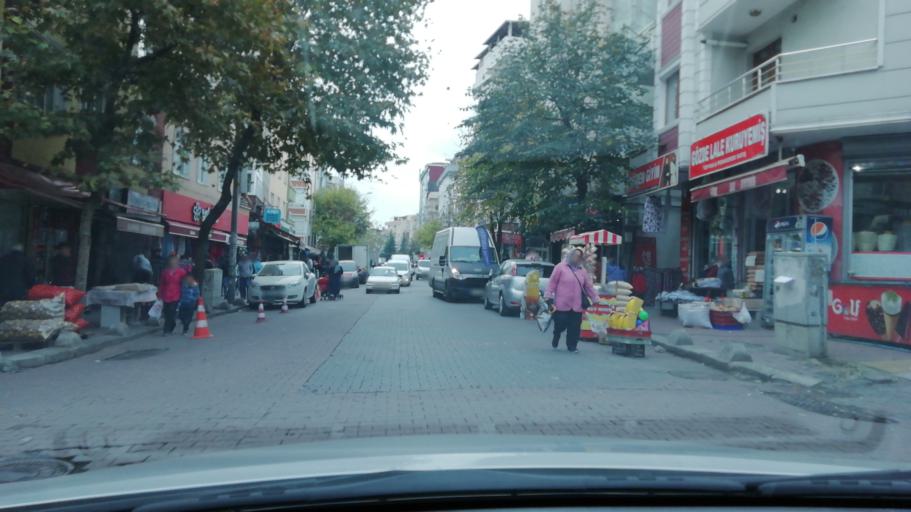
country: TR
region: Istanbul
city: Bahcelievler
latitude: 41.0098
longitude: 28.8333
